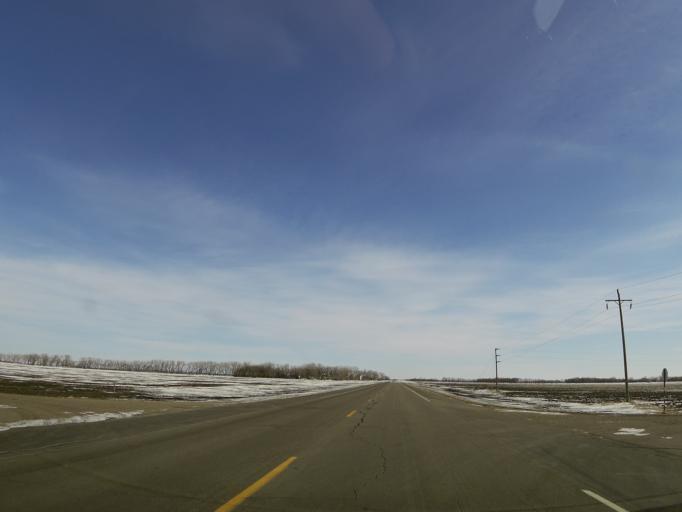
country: US
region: North Dakota
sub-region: Walsh County
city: Grafton
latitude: 48.4120
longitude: -97.2342
